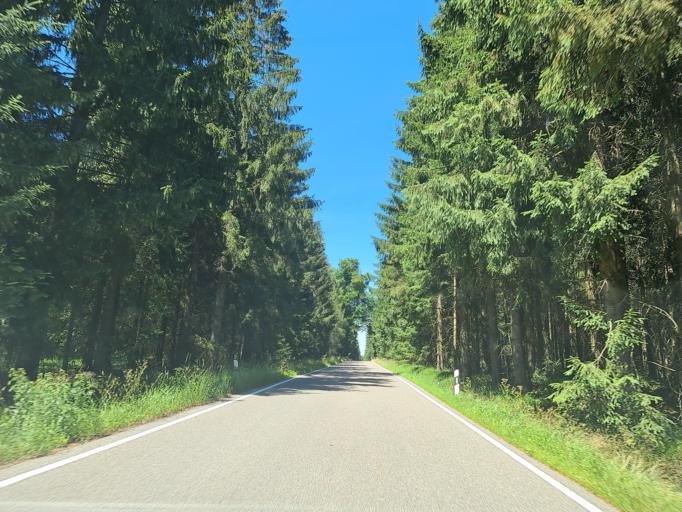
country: DE
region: Saxony
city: Rechenberg-Bienenmuhle
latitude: 50.7163
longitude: 13.5317
